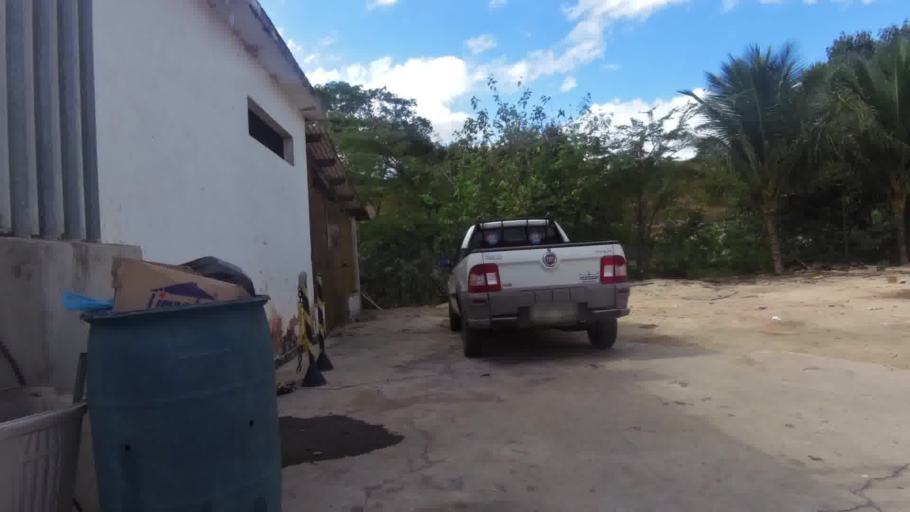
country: BR
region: Espirito Santo
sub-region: Marataizes
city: Marataizes
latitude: -21.1029
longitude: -41.0421
